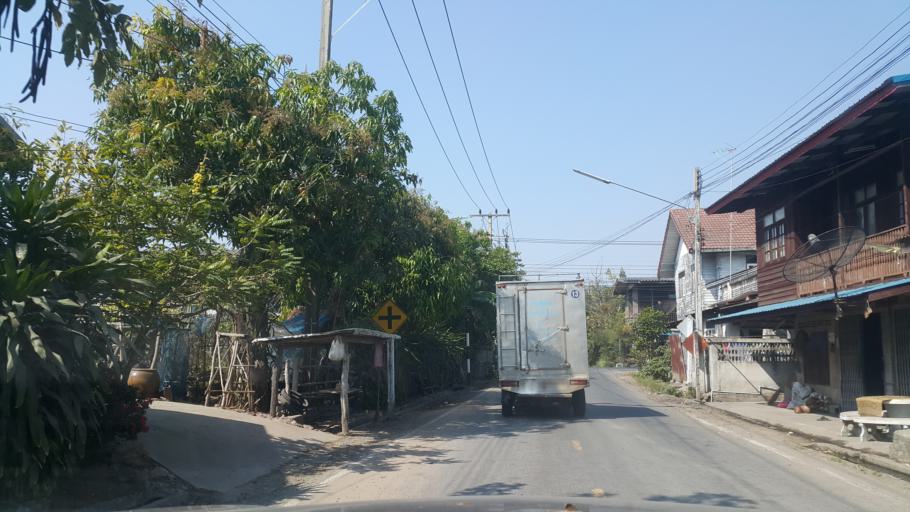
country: TH
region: Buriram
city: Krasang
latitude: 15.0540
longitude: 103.3840
